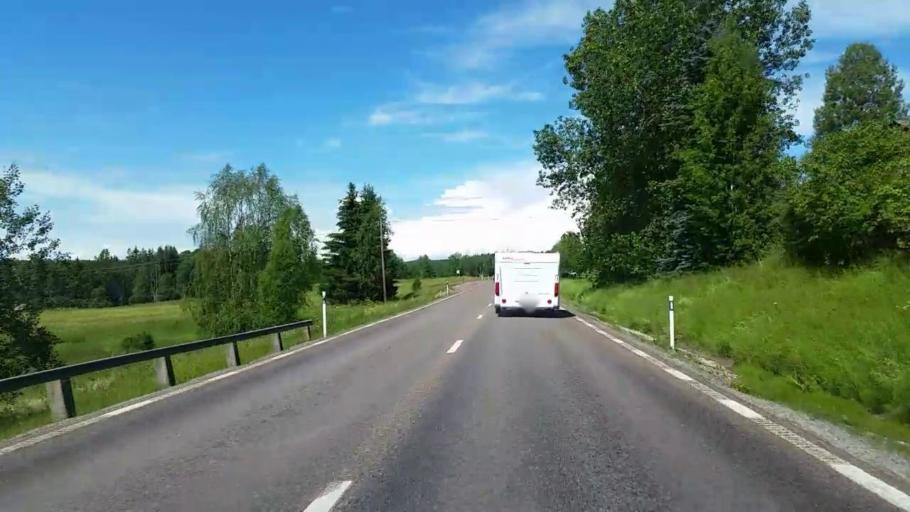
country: SE
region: Dalarna
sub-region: Rattviks Kommun
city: Raettvik
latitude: 60.9886
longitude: 15.2198
